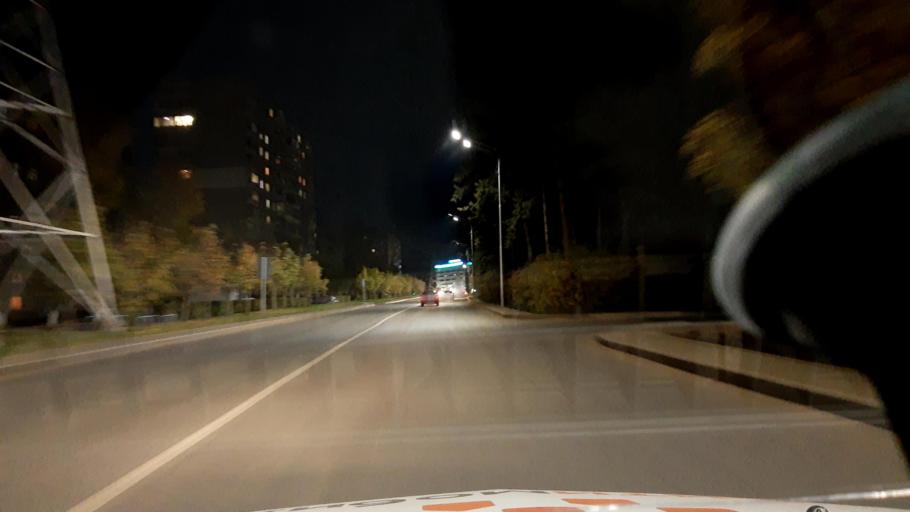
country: RU
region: Bashkortostan
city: Ufa
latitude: 54.7041
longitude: 56.0074
